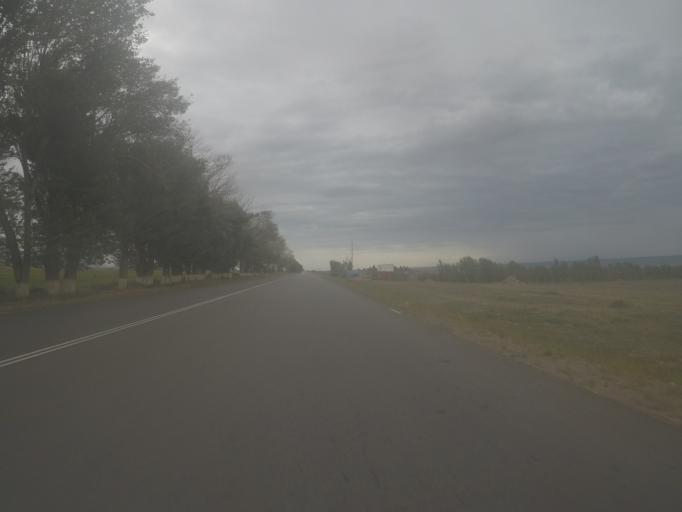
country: KG
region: Ysyk-Koel
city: Cholpon-Ata
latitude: 42.5987
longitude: 76.7940
